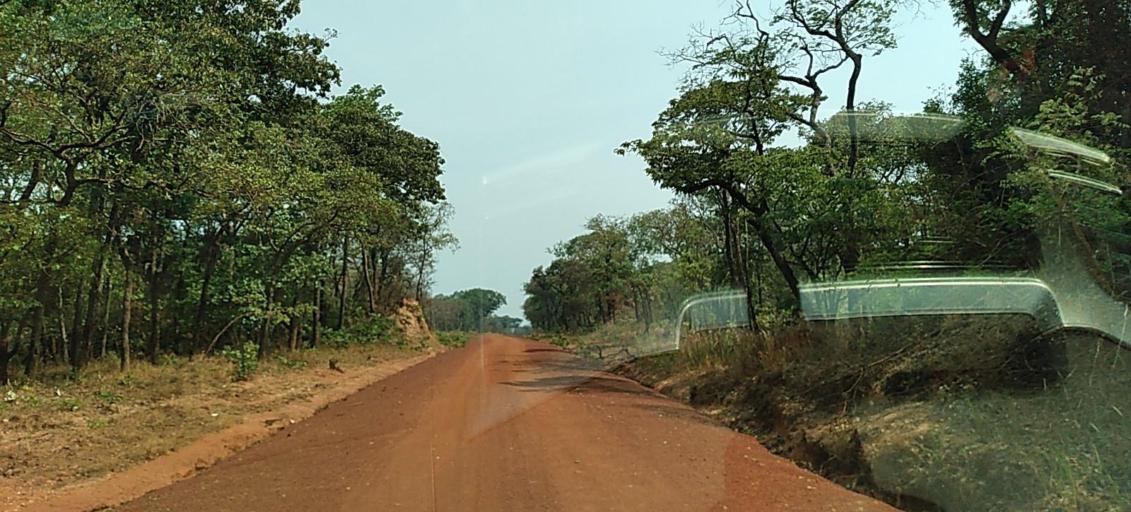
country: ZM
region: North-Western
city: Kansanshi
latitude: -12.0136
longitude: 26.8469
